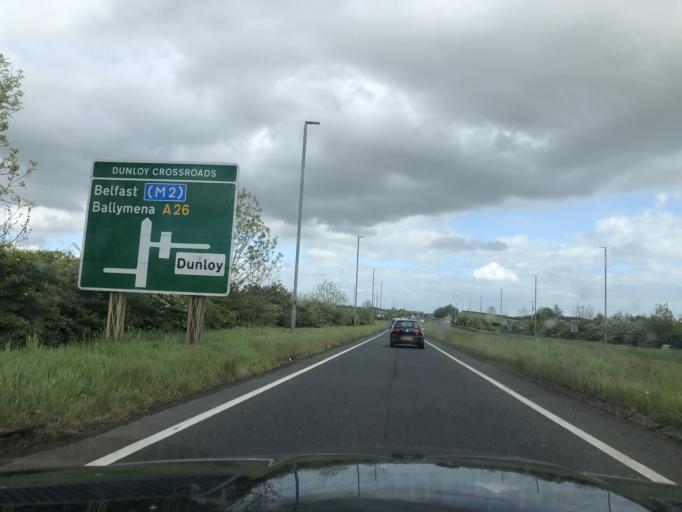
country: GB
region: Northern Ireland
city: Dunloy
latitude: 55.0255
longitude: -6.3874
